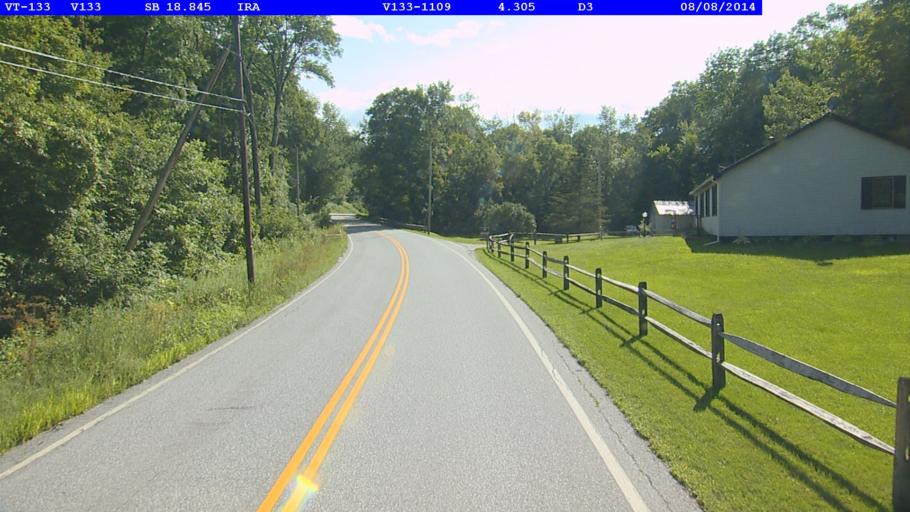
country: US
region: Vermont
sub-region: Rutland County
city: West Rutland
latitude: 43.5463
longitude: -73.0447
